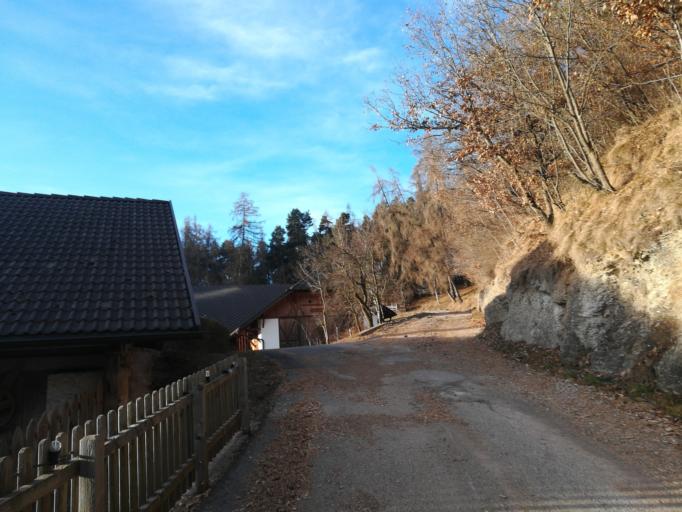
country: IT
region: Trentino-Alto Adige
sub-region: Bolzano
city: Collalbo
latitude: 46.5372
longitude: 11.4567
